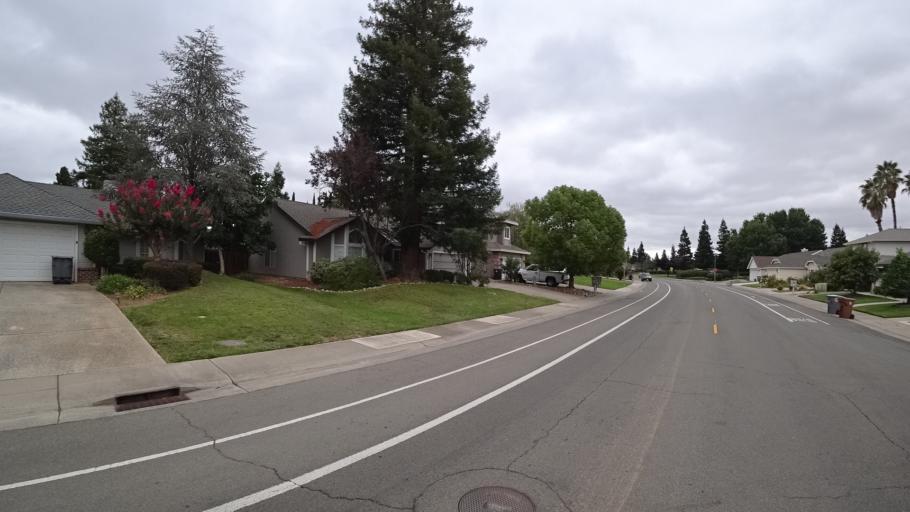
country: US
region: California
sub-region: Sacramento County
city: Laguna
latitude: 38.4214
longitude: -121.4380
